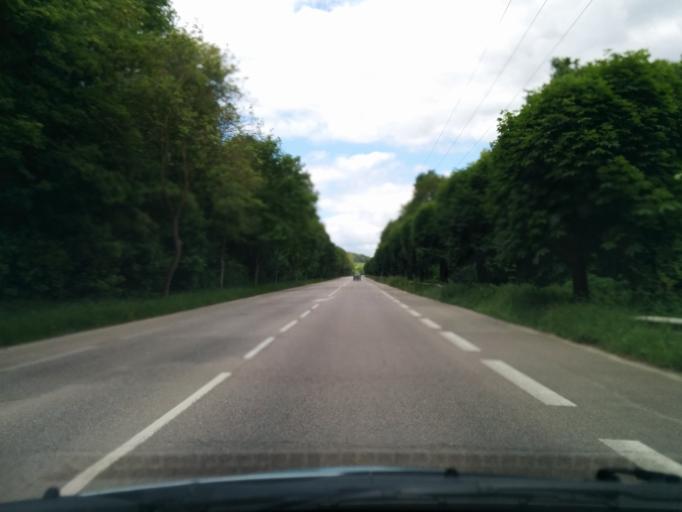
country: FR
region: Ile-de-France
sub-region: Departement des Yvelines
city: Porcheville
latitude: 48.9626
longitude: 1.7691
